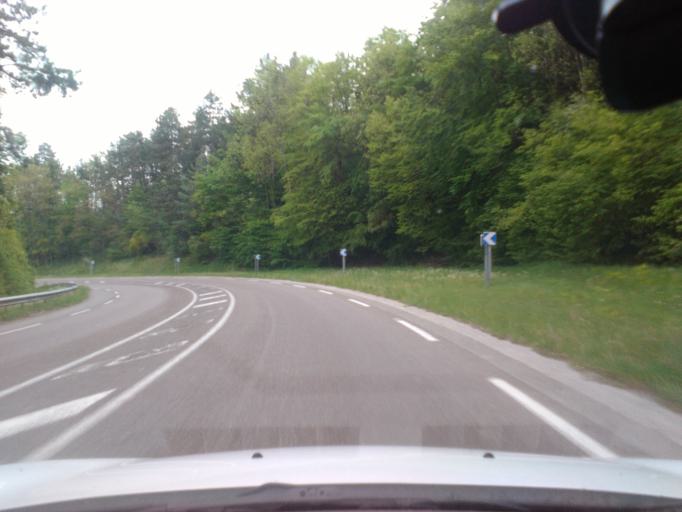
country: FR
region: Champagne-Ardenne
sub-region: Departement de la Haute-Marne
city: Chaumont
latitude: 48.1376
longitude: 5.0495
